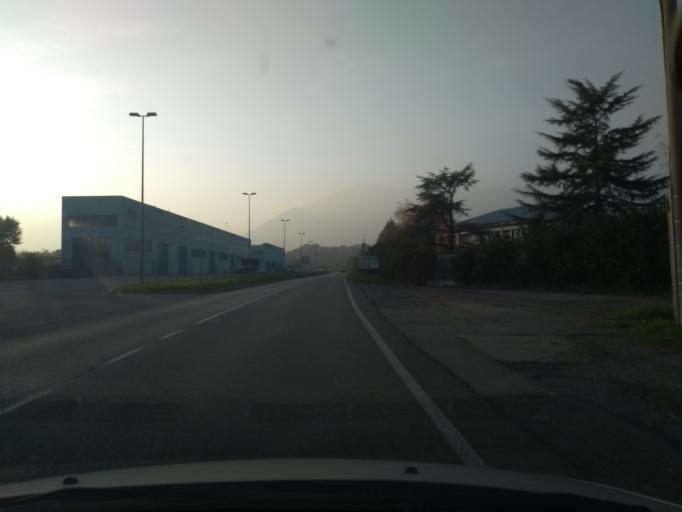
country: IT
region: Piedmont
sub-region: Provincia di Torino
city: San Gillio
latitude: 45.1514
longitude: 7.5281
